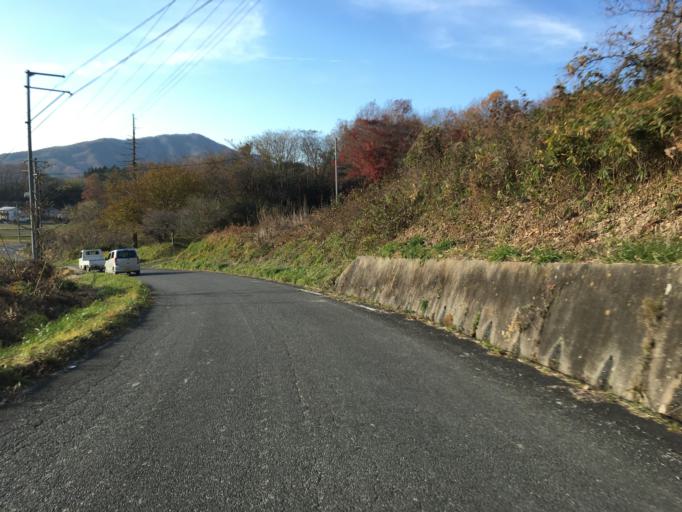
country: JP
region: Fukushima
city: Ishikawa
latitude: 37.2492
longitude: 140.5741
